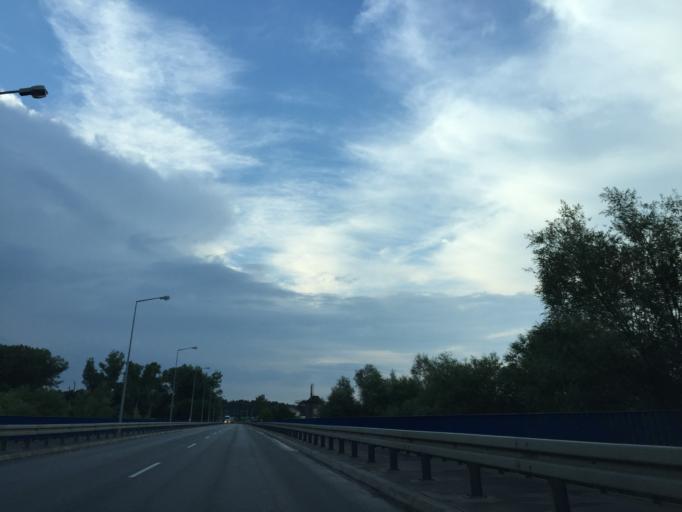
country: PL
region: Masovian Voivodeship
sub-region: Powiat ostrowski
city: Brok
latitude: 52.6939
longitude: 21.8500
